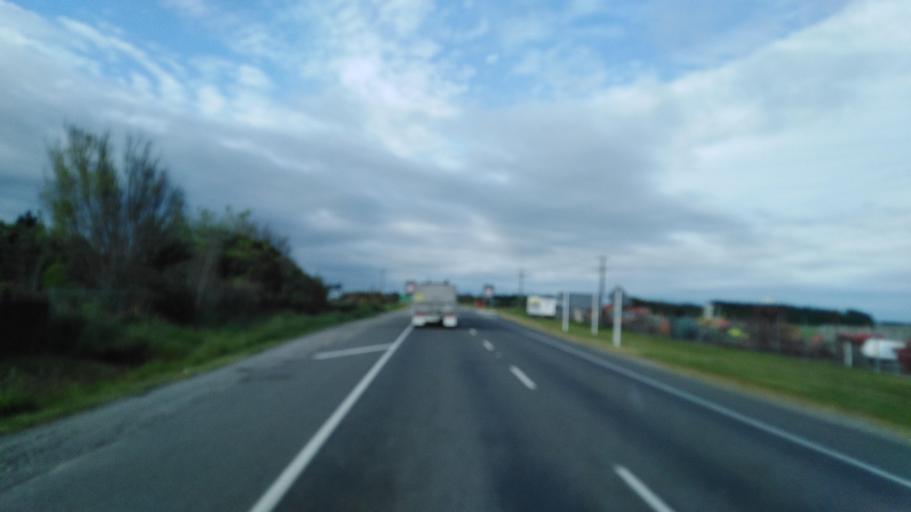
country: NZ
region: Manawatu-Wanganui
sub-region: Rangitikei District
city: Bulls
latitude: -40.2214
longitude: 175.4231
